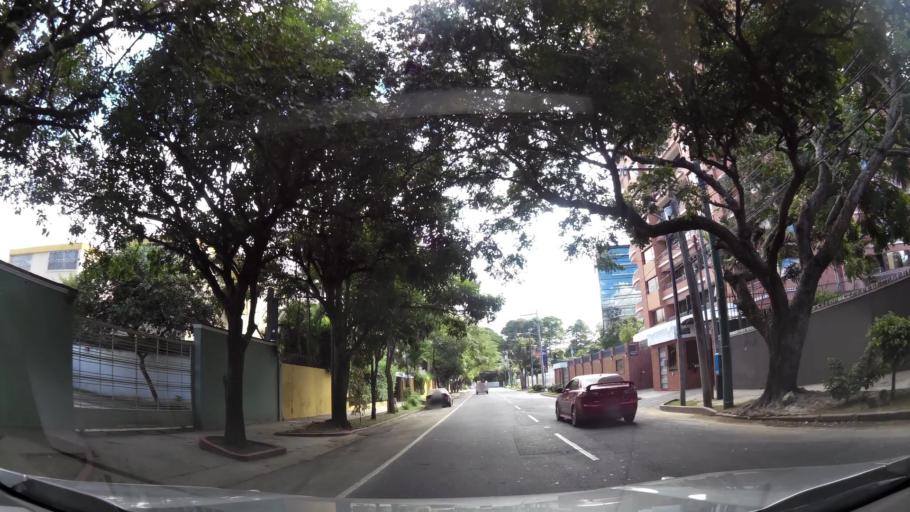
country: GT
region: Guatemala
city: Santa Catarina Pinula
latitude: 14.6001
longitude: -90.5102
